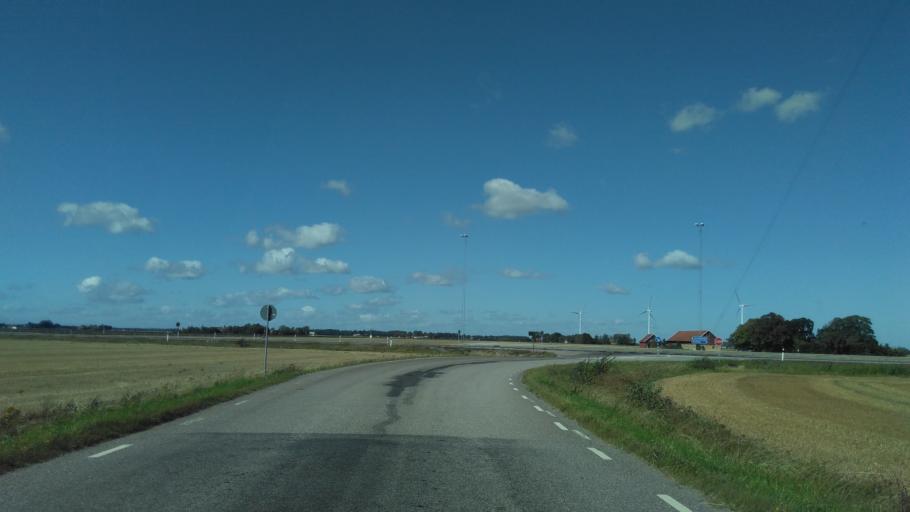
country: SE
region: Vaestra Goetaland
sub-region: Vara Kommun
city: Vara
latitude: 58.2693
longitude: 13.0089
